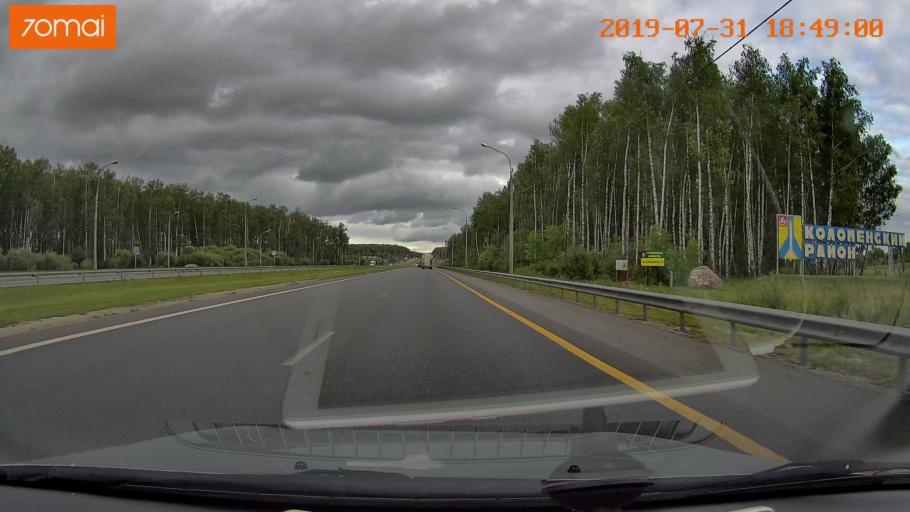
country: RU
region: Moskovskaya
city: Troitskoye
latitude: 55.2348
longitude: 38.5501
